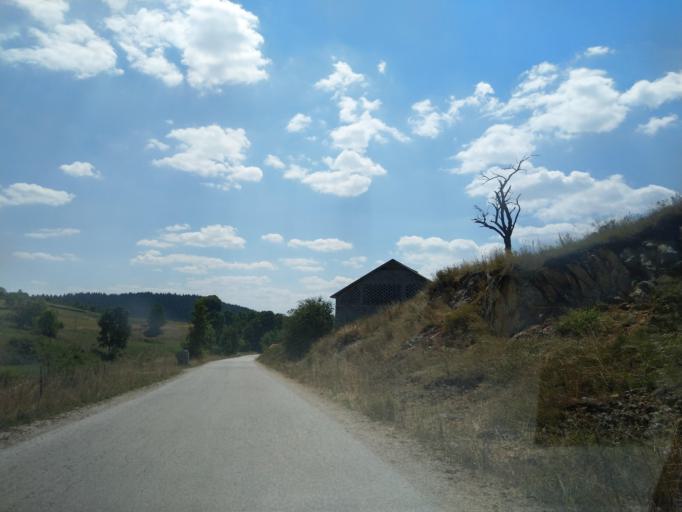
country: RS
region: Central Serbia
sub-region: Zlatiborski Okrug
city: Nova Varos
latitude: 43.4566
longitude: 19.9722
